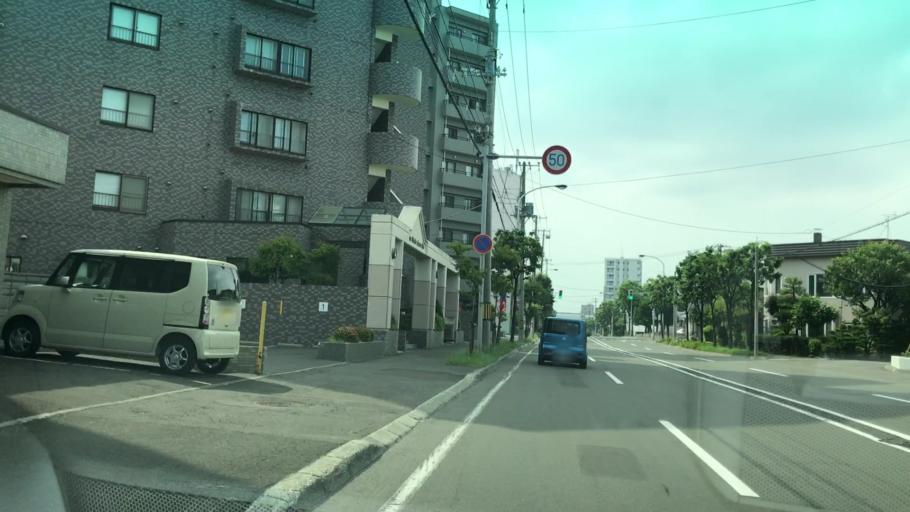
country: JP
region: Hokkaido
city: Sapporo
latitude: 43.0904
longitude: 141.2888
